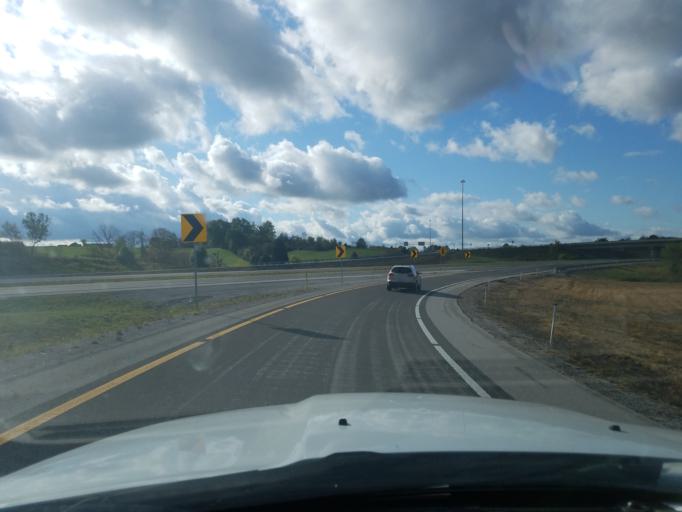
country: US
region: Kentucky
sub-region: Pulaski County
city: Somerset
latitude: 37.1071
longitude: -84.6612
